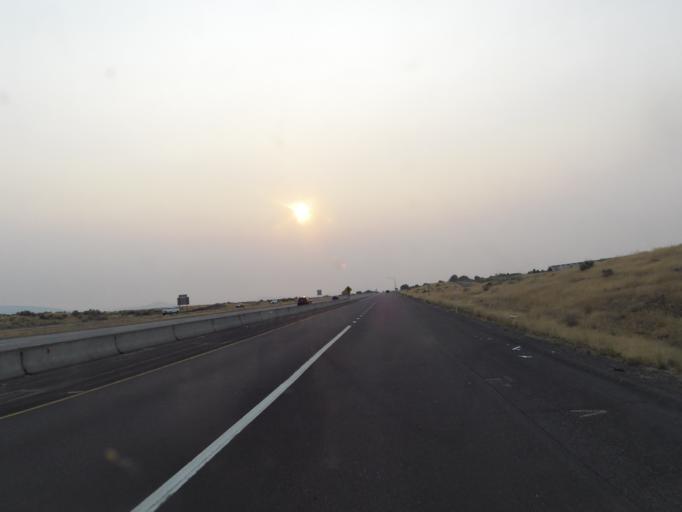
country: US
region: Washington
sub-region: Franklin County
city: West Pasco
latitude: 46.2675
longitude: -119.1873
